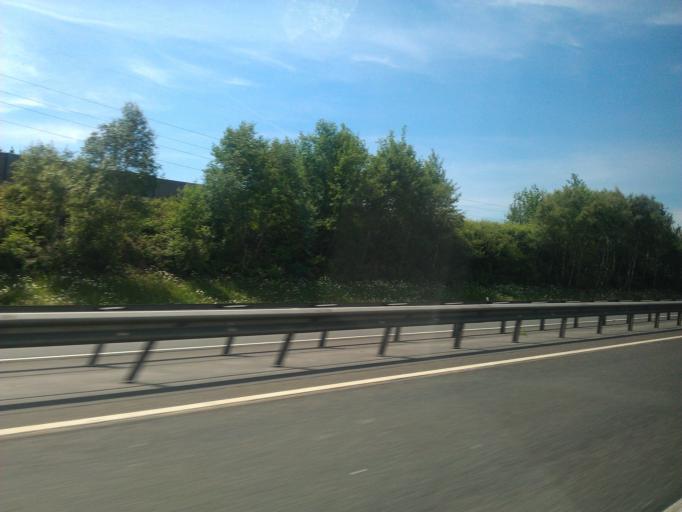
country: DE
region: Rheinland-Pfalz
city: Obersteinebach
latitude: 50.5871
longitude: 7.4591
